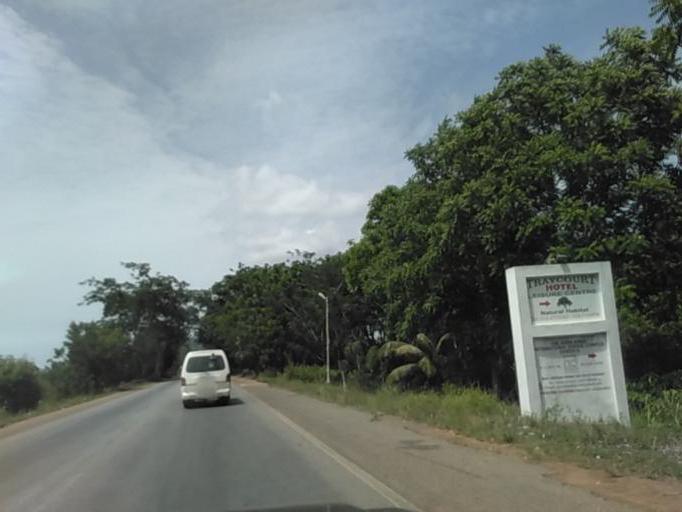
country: GH
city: Akropong
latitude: 6.1193
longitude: 0.0485
